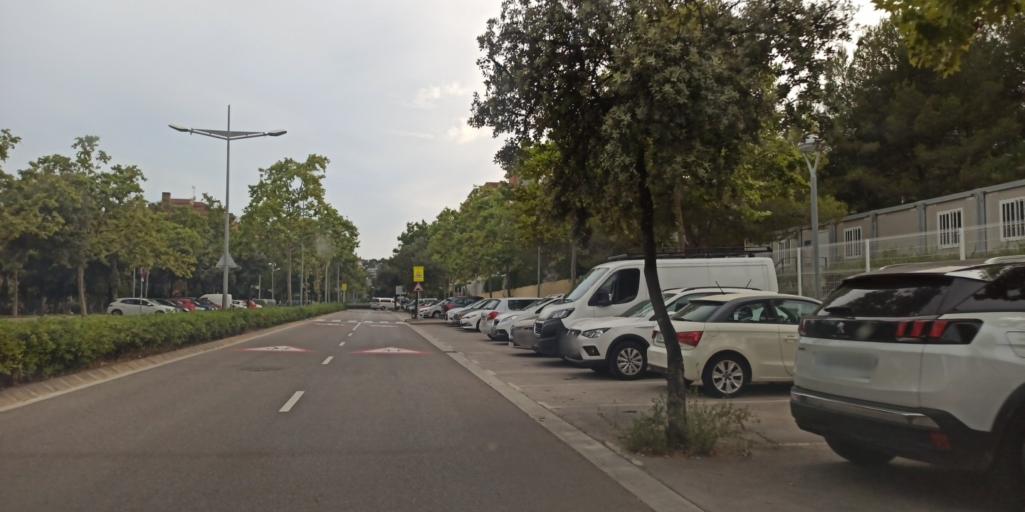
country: ES
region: Catalonia
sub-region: Provincia de Barcelona
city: Castelldefels
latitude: 41.2820
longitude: 1.9721
